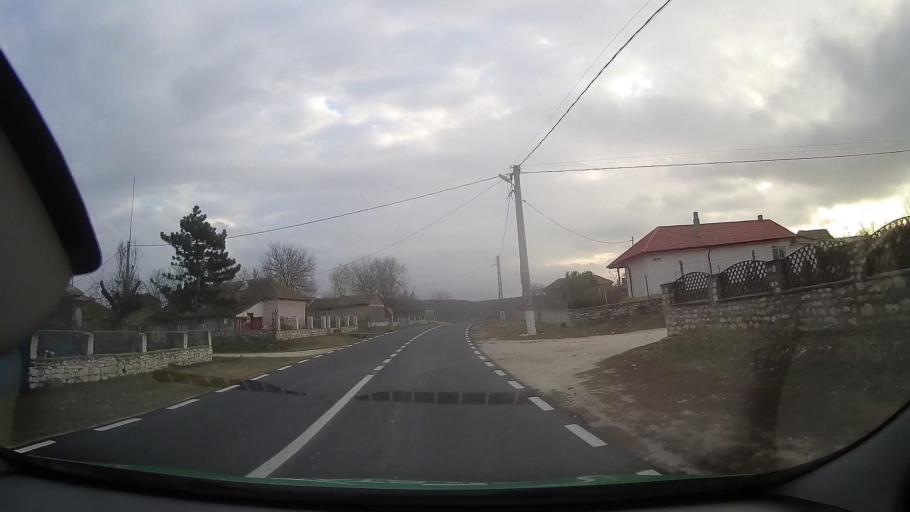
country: RO
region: Constanta
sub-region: Comuna Adamclisi
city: Adamclisi
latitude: 44.0477
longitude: 27.9614
